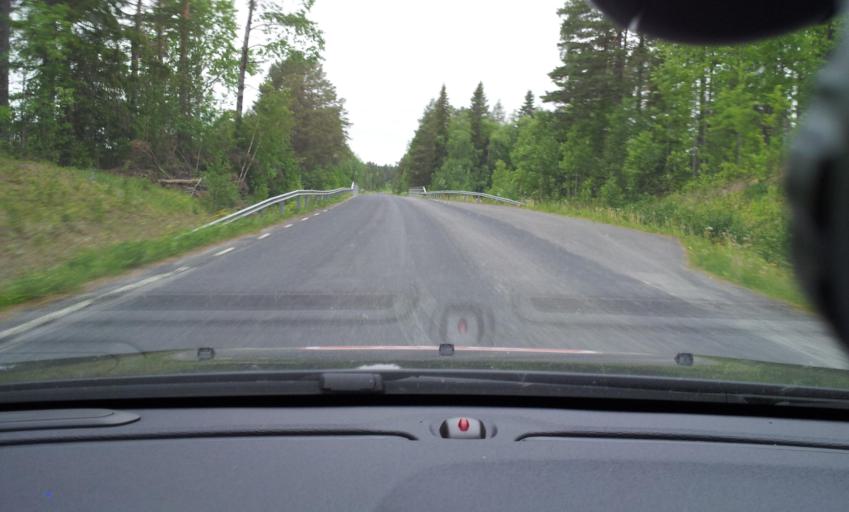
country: SE
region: Jaemtland
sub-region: Krokoms Kommun
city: Valla
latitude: 63.2850
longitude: 13.8888
